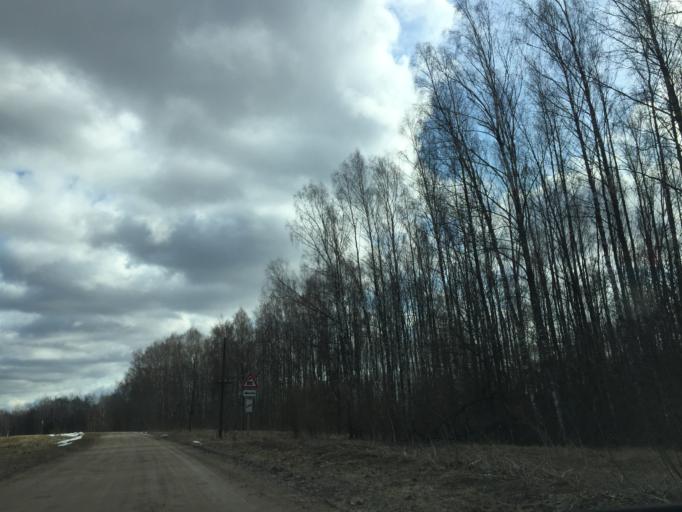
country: LV
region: Vecumnieki
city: Vecumnieki
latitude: 56.5834
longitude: 24.5932
